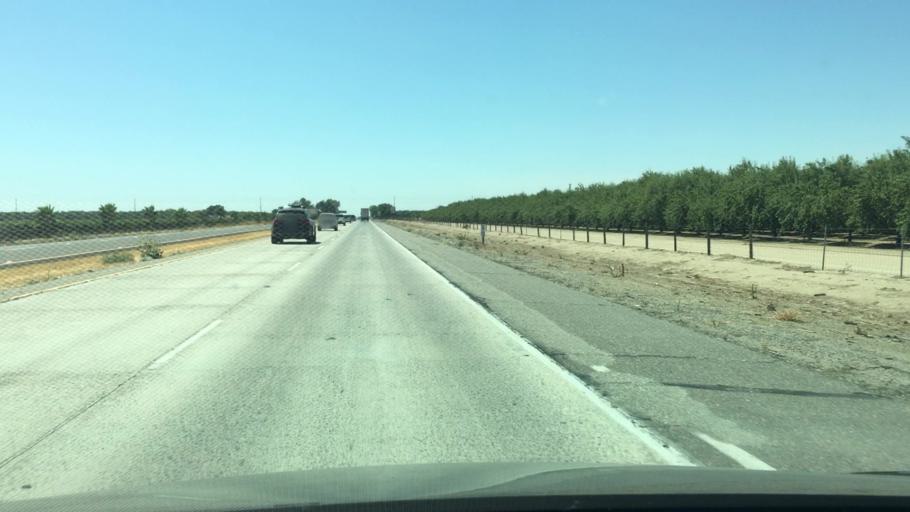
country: US
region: California
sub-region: Madera County
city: Chowchilla
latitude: 37.0836
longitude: -120.3021
